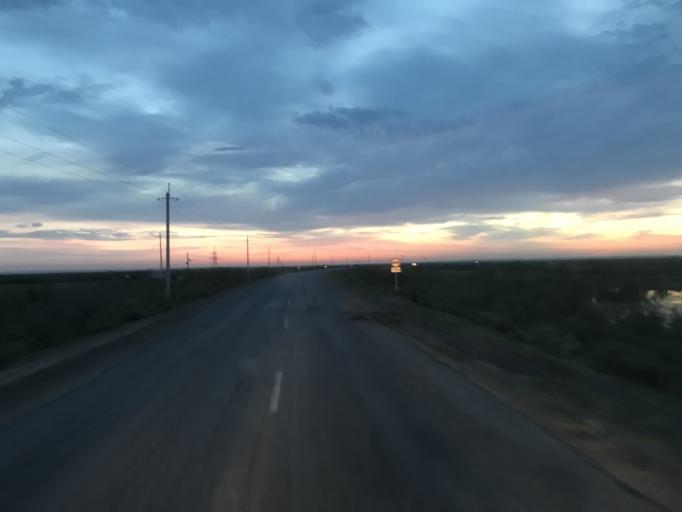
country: KZ
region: Ongtustik Qazaqstan
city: Asykata
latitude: 41.0018
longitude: 68.4701
